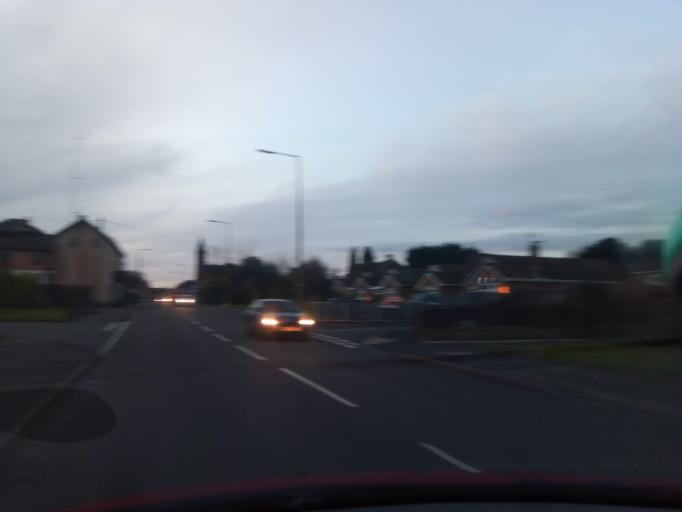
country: GB
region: England
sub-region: Derbyshire
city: Borrowash
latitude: 52.9057
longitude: -1.3780
